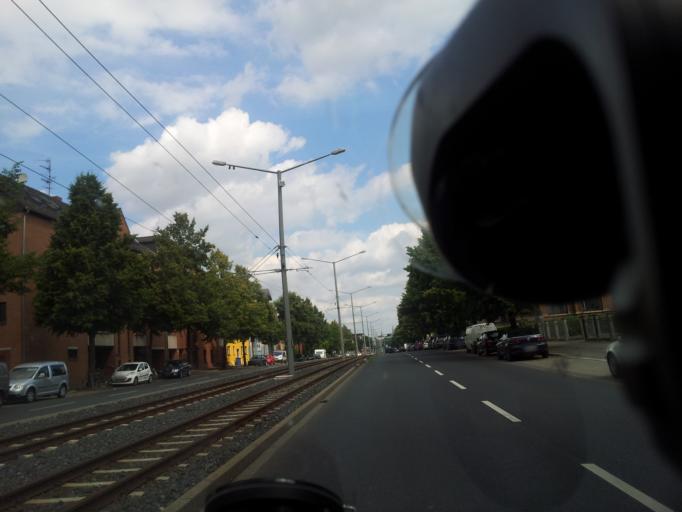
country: DE
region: Lower Saxony
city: Braunschweig
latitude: 52.2520
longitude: 10.5290
